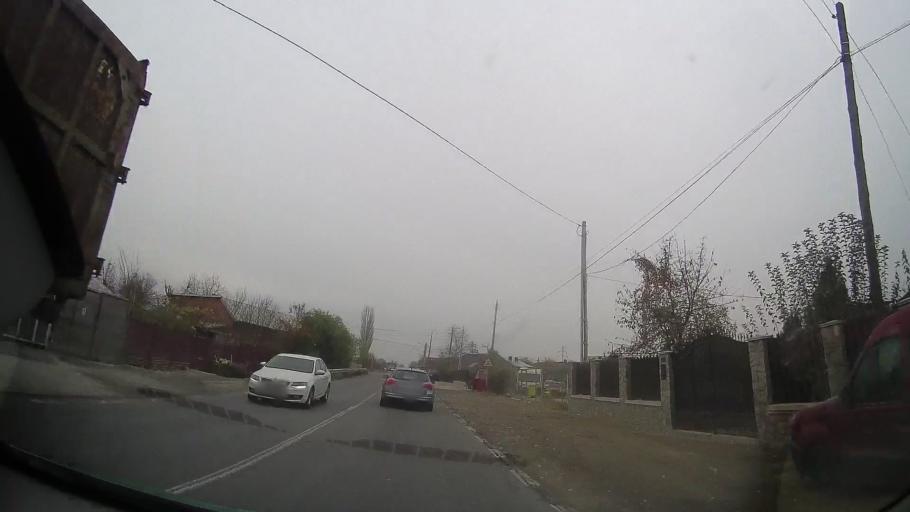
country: RO
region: Prahova
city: Ploiesti
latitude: 44.9637
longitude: 26.0338
